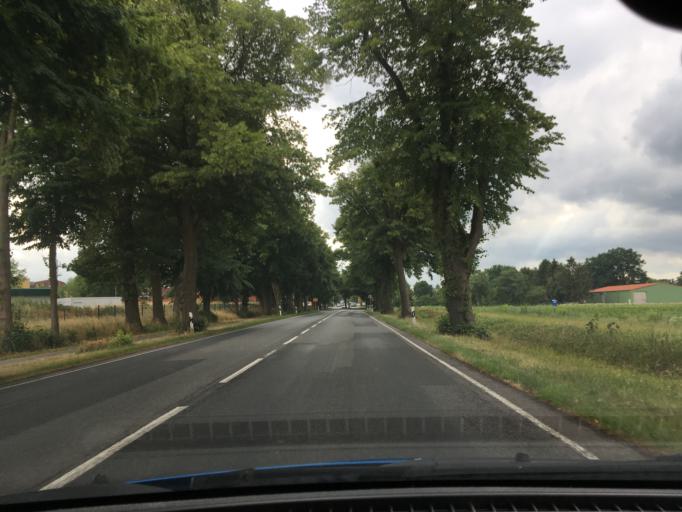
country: DE
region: Lower Saxony
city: Tostedt
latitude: 53.2855
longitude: 9.7200
